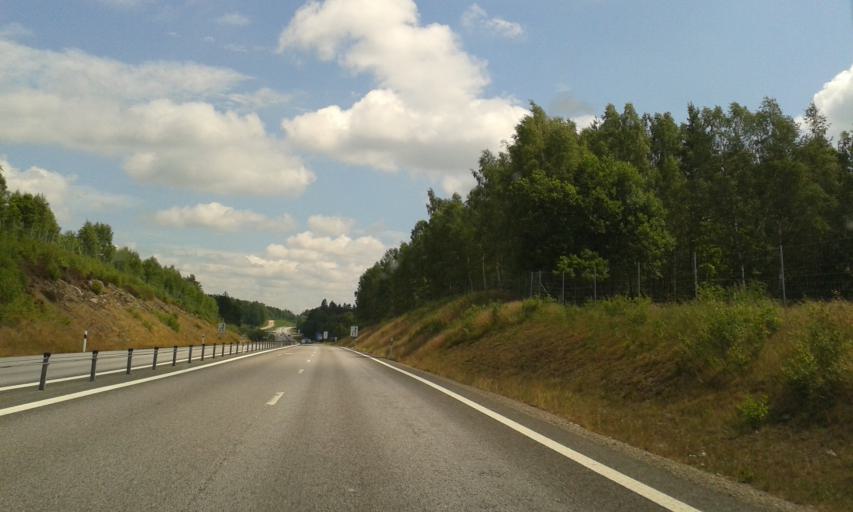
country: SE
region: Kronoberg
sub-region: Alvesta Kommun
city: Alvesta
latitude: 56.9207
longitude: 14.5817
